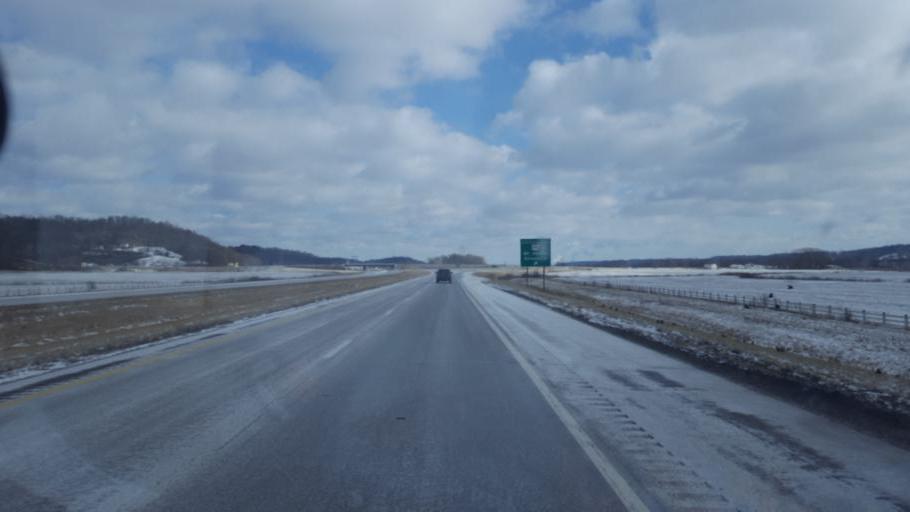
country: US
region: Ohio
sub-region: Muskingum County
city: Frazeysburg
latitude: 40.0997
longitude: -82.1834
